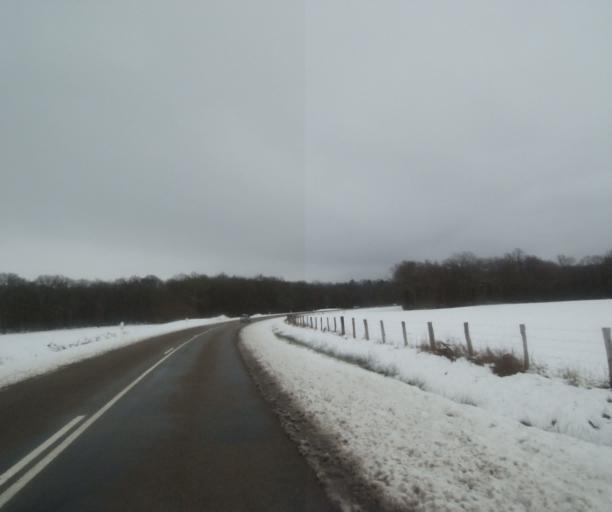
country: FR
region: Champagne-Ardenne
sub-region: Departement de la Haute-Marne
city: Montier-en-Der
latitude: 48.4779
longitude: 4.7874
